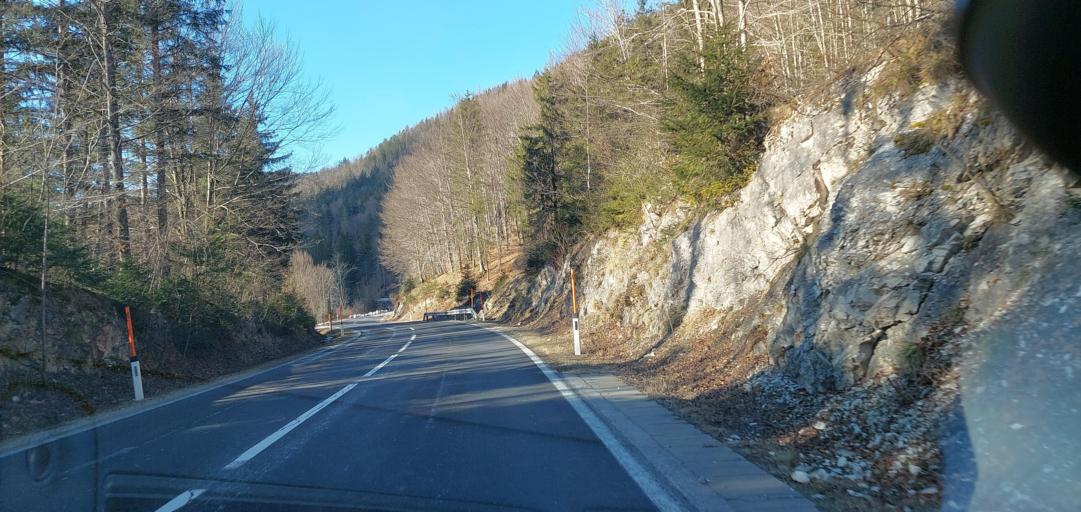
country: AT
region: Upper Austria
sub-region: Politischer Bezirk Gmunden
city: Bad Ischl
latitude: 47.7647
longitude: 13.6450
